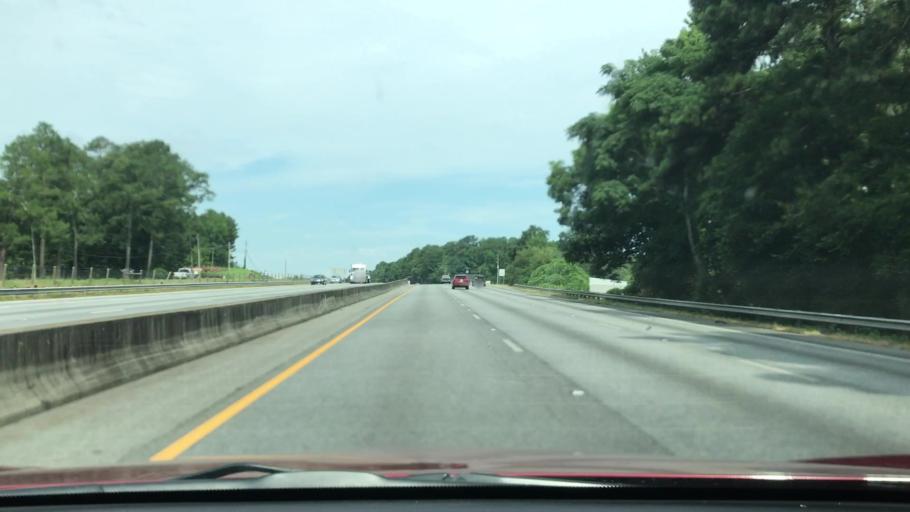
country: US
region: Georgia
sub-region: Newton County
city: Oxford
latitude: 33.6110
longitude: -83.8884
